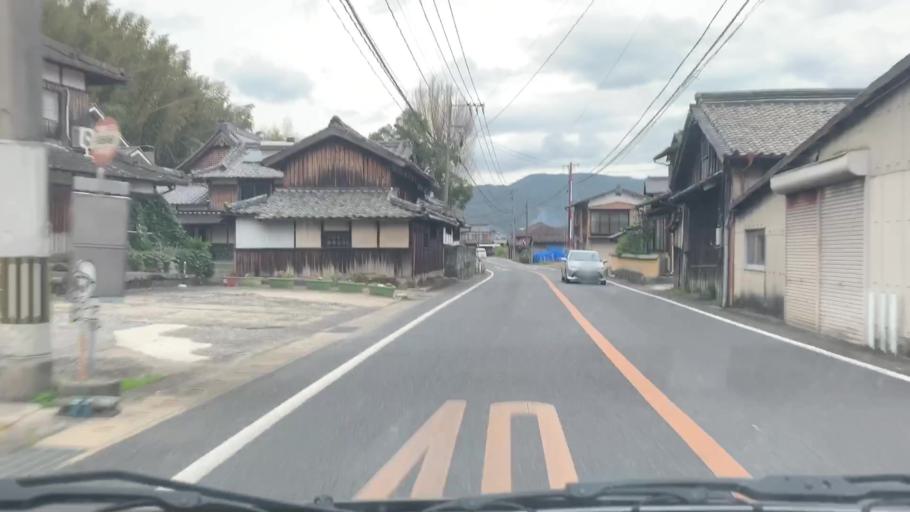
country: JP
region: Saga Prefecture
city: Kashima
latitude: 33.1372
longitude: 130.0636
